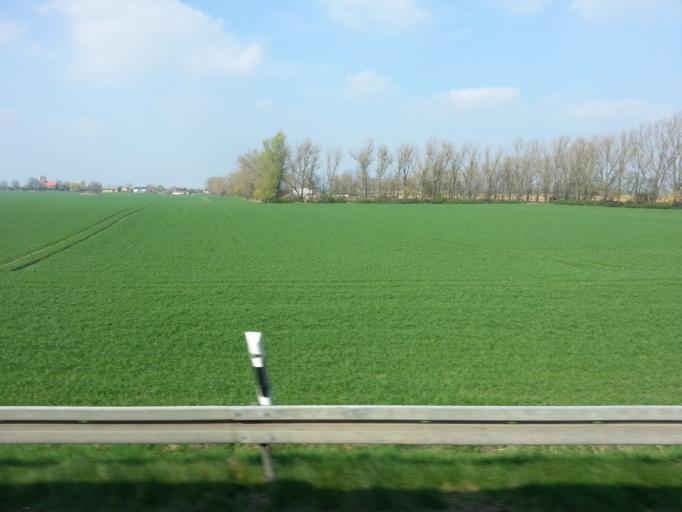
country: DE
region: Brandenburg
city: Fehrbellin
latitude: 52.7483
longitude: 12.8849
